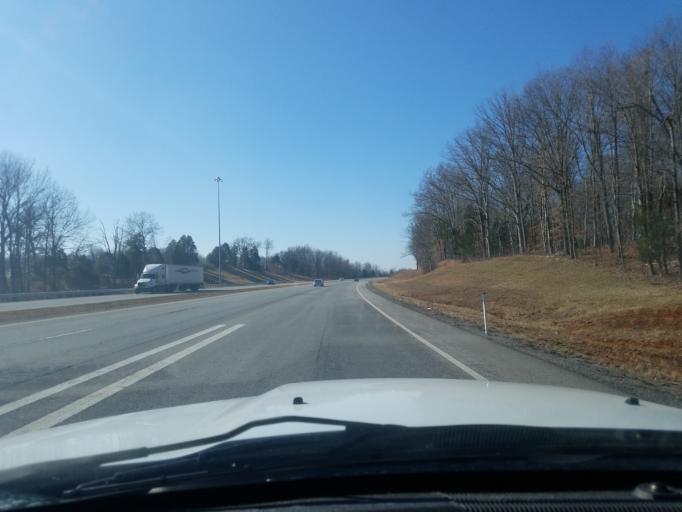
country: US
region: Kentucky
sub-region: Hardin County
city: Elizabethtown
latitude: 37.6513
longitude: -85.8946
